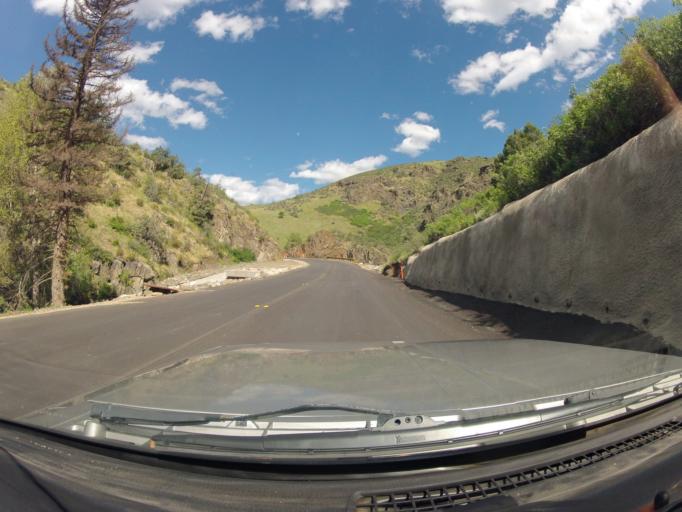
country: US
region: Colorado
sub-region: Larimer County
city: Laporte
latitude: 40.5637
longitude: -105.3040
